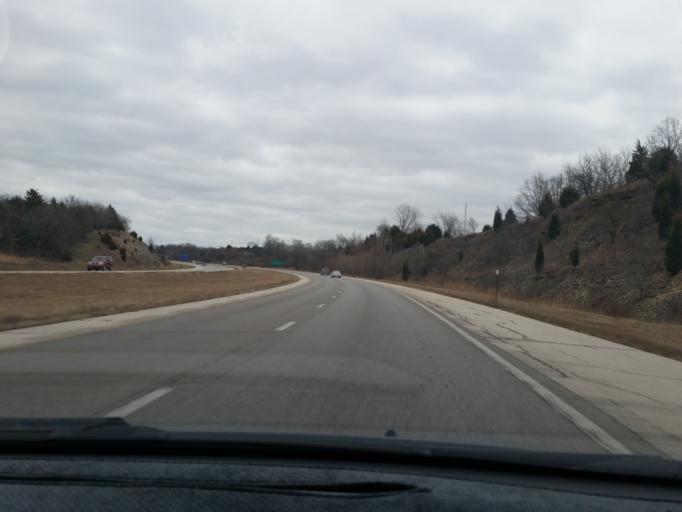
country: US
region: Kansas
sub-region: Johnson County
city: De Soto
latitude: 38.9481
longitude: -94.9007
